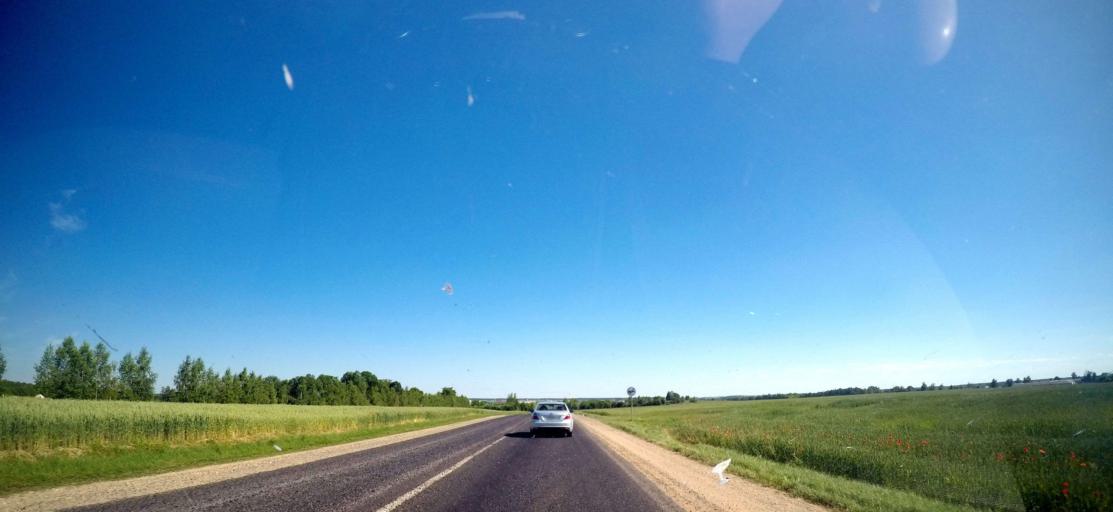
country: BY
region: Grodnenskaya
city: Vyalikaya Byerastavitsa
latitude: 53.2148
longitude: 24.0010
